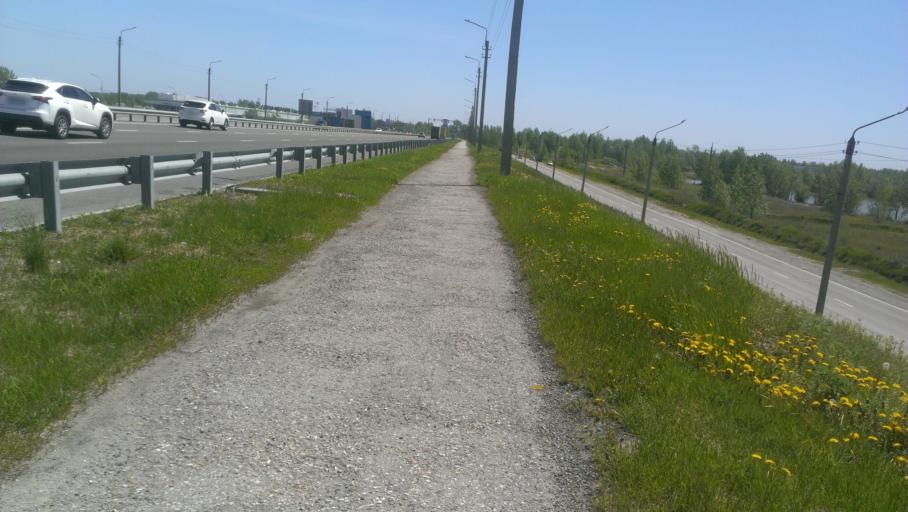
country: RU
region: Altai Krai
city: Zaton
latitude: 53.3185
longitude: 83.8177
